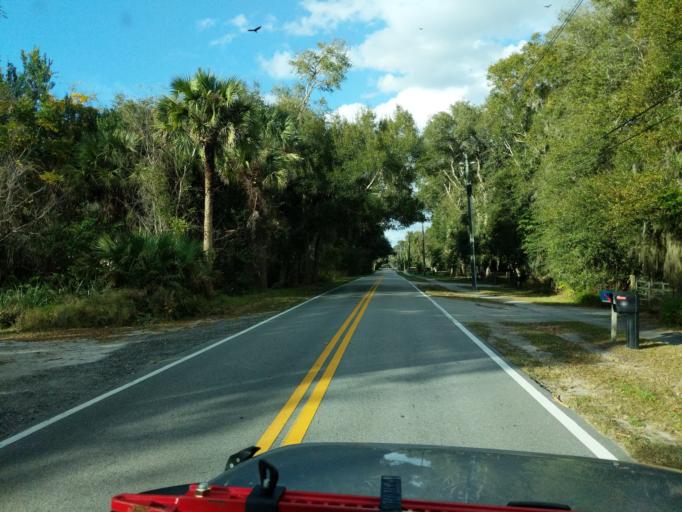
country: US
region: Florida
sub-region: Seminole County
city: Geneva
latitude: 28.7489
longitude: -81.1195
